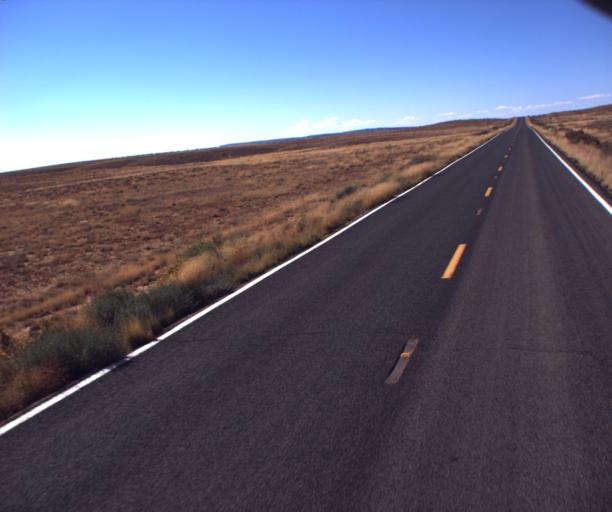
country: US
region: Arizona
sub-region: Navajo County
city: First Mesa
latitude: 35.9778
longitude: -110.7488
